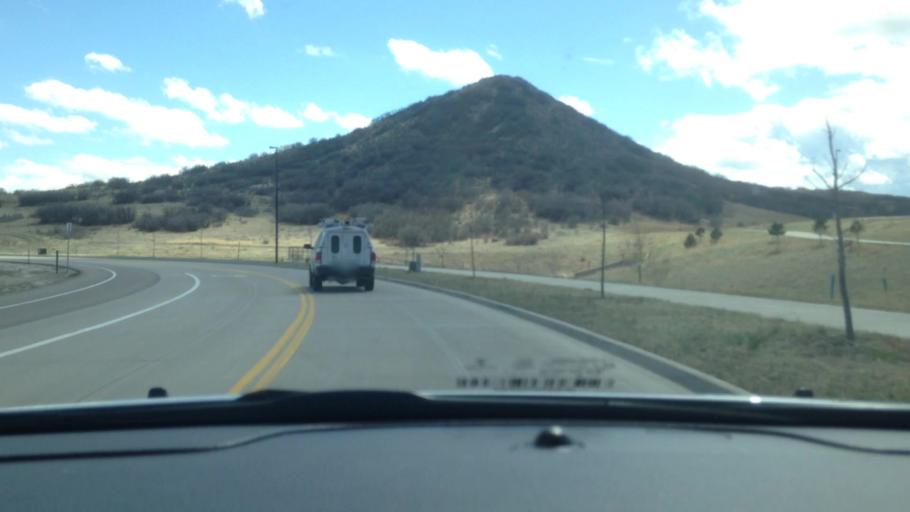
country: US
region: Colorado
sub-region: Douglas County
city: Castle Rock
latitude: 39.3708
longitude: -104.8774
